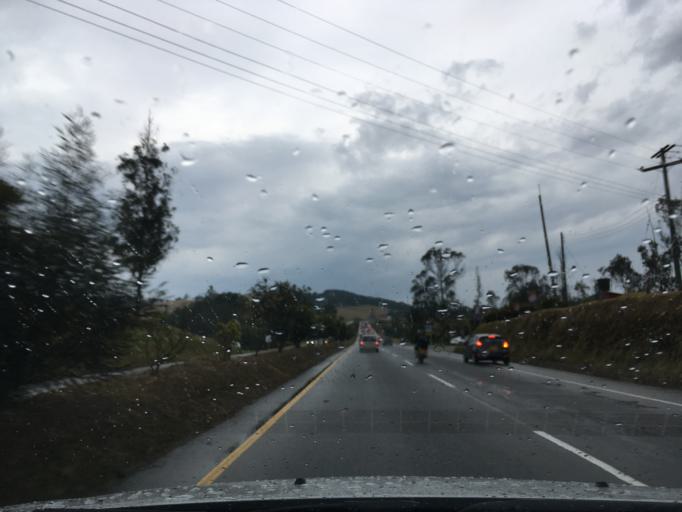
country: CO
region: Cundinamarca
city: Choconta
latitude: 5.1040
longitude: -73.7043
